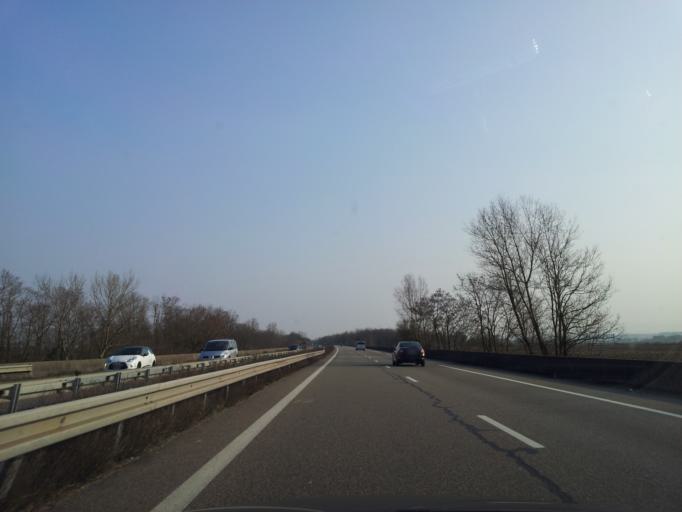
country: FR
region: Alsace
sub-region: Departement du Haut-Rhin
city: Blotzheim
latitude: 47.6286
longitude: 7.5055
